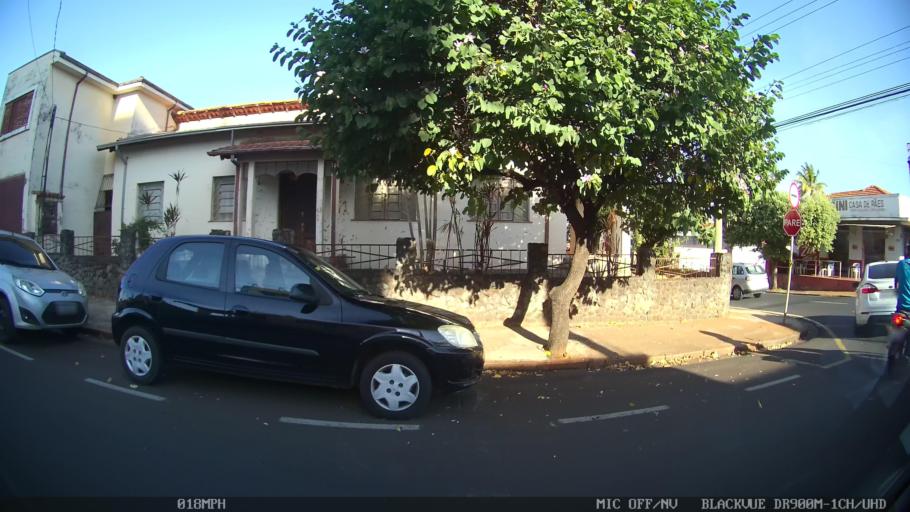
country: BR
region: Sao Paulo
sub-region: Sao Jose Do Rio Preto
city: Sao Jose do Rio Preto
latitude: -20.8109
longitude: -49.3896
